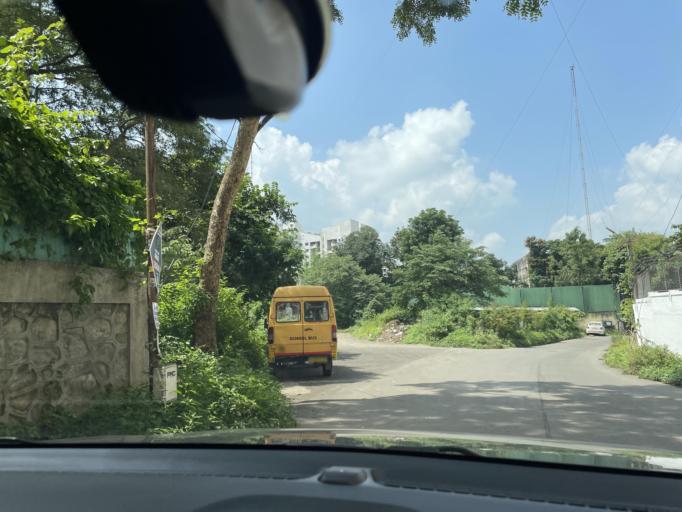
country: IN
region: Maharashtra
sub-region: Pune Division
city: Kharakvasla
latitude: 18.5099
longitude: 73.7801
